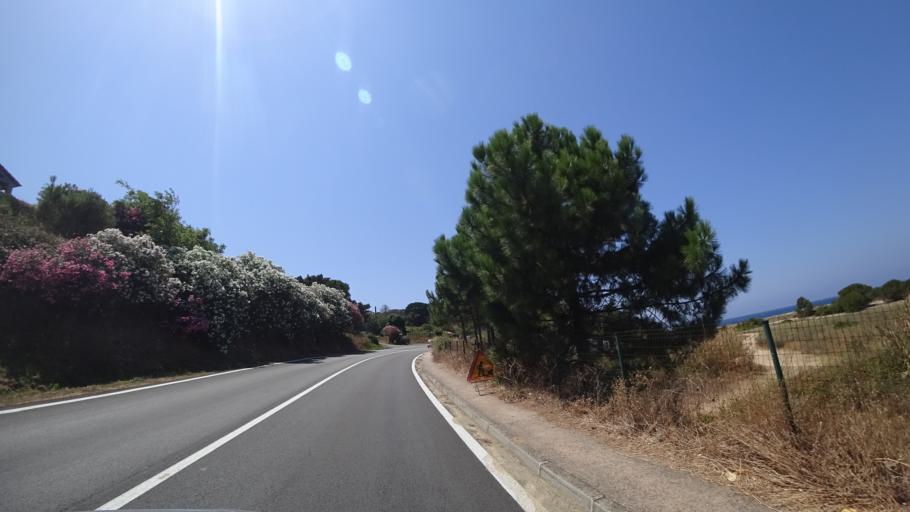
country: FR
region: Corsica
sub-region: Departement de la Corse-du-Sud
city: Propriano
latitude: 41.6830
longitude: 8.9205
